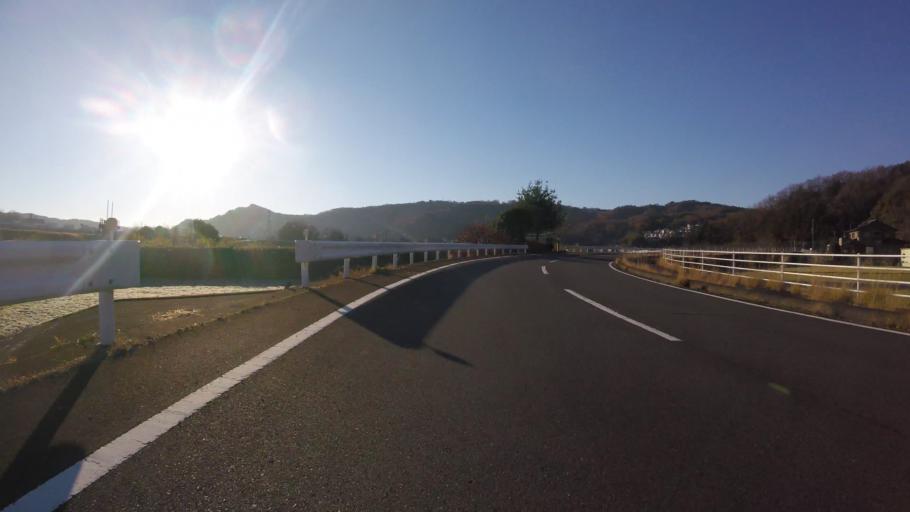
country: JP
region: Shizuoka
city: Mishima
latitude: 34.9972
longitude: 138.9310
